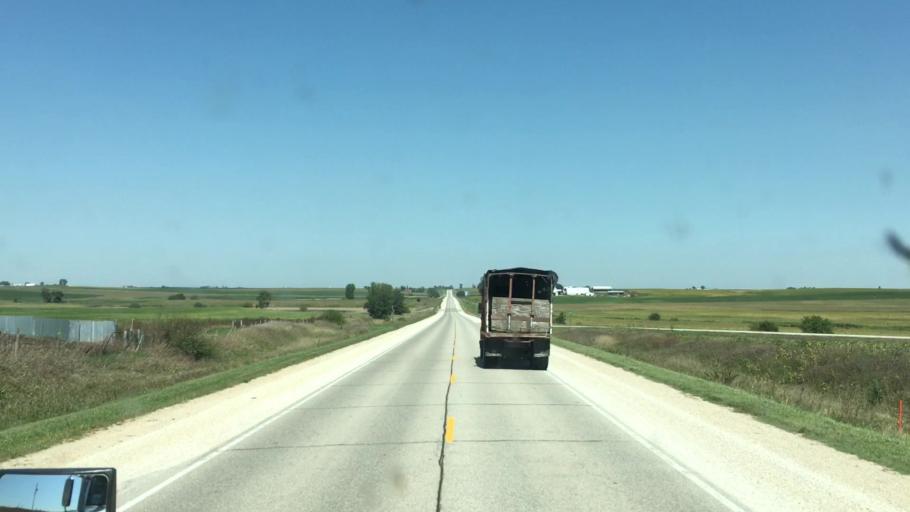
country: US
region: Iowa
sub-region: Tama County
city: Dysart
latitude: 42.0639
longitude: -92.2988
